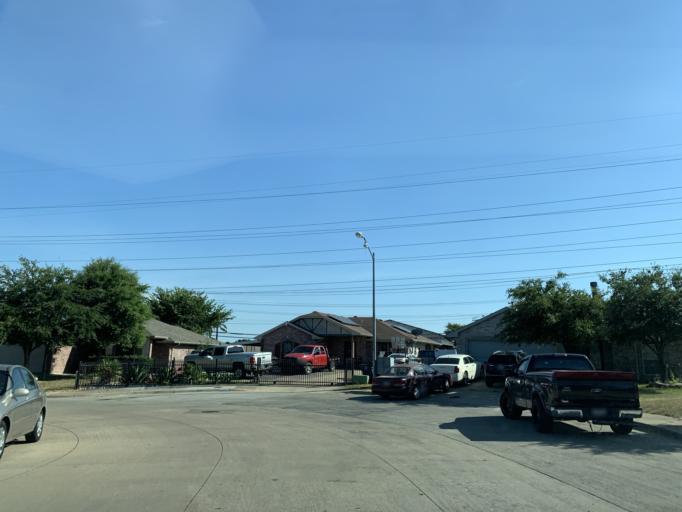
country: US
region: Texas
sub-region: Dallas County
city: Cockrell Hill
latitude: 32.7065
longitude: -96.8954
